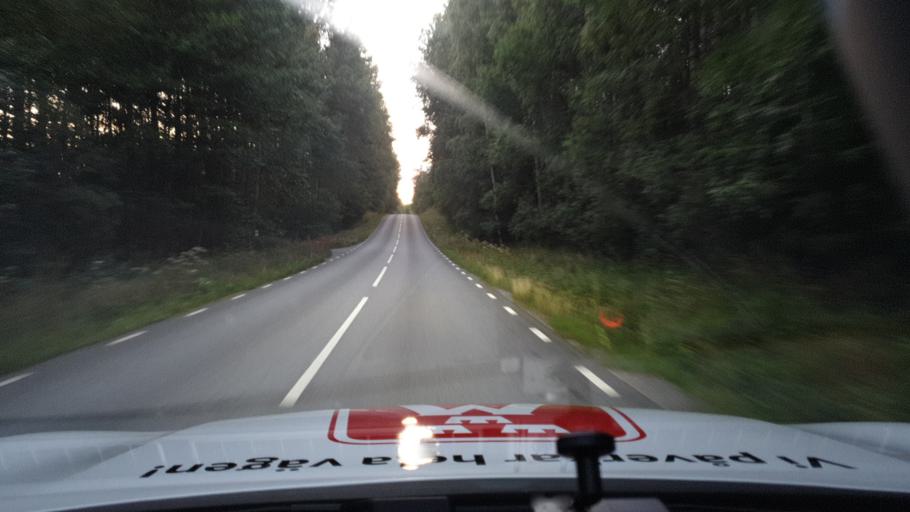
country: SE
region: Vaestmanland
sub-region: Kopings Kommun
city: Kolsva
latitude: 59.7247
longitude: 15.8323
